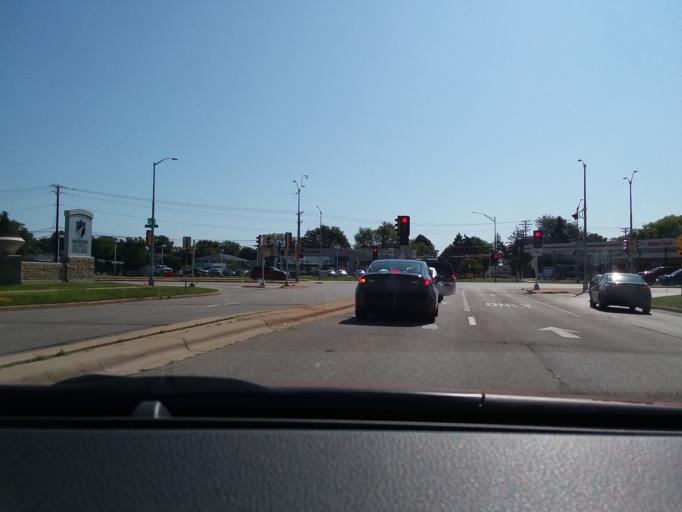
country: US
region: Wisconsin
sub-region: Dane County
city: Maple Bluff
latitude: 43.1210
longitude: -89.3257
